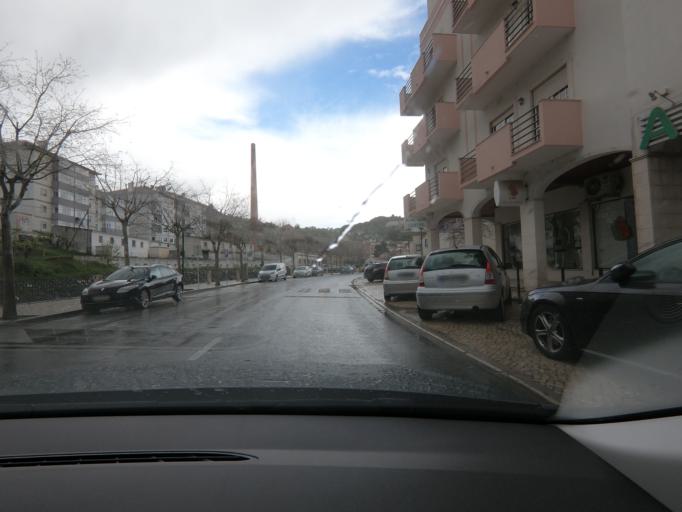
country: PT
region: Lisbon
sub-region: Alenquer
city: Alenquer
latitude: 39.0501
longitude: -9.0060
